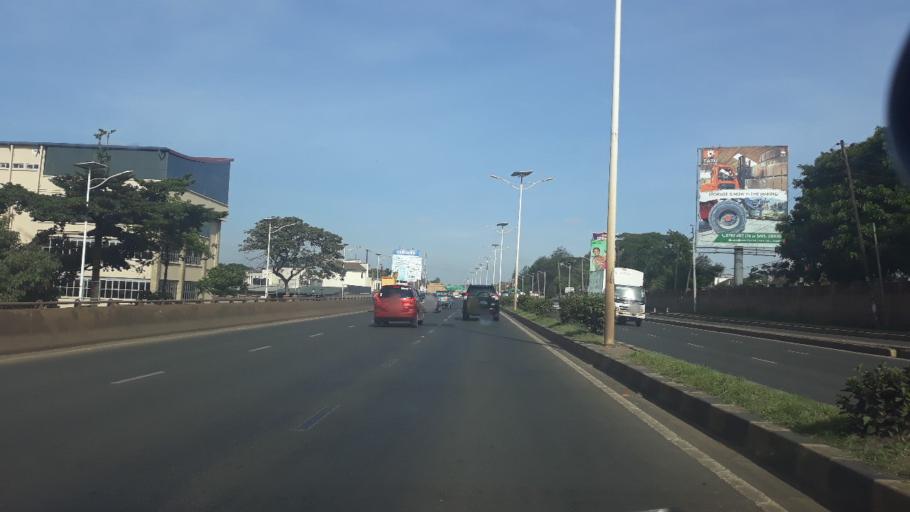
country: KE
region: Nairobi Area
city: Nairobi
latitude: -1.2685
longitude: 36.8262
